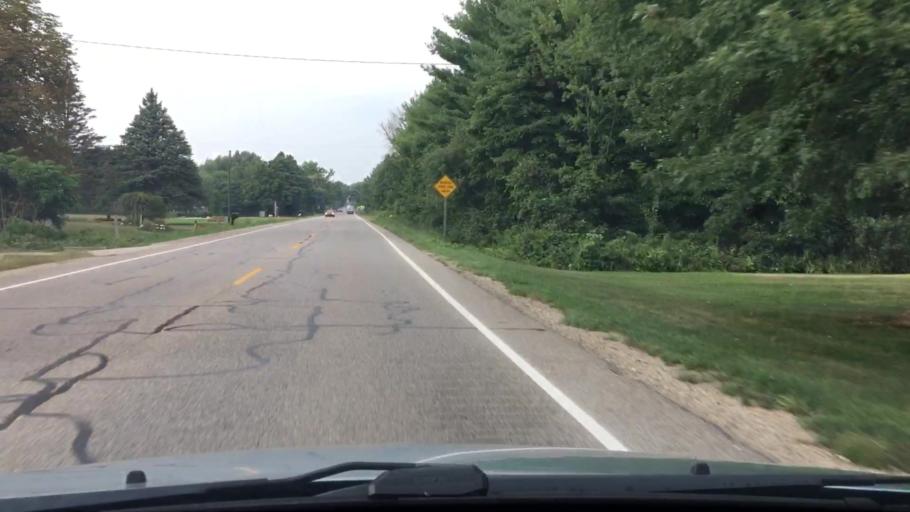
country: US
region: Michigan
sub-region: Ottawa County
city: Hudsonville
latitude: 42.9103
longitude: -85.9023
